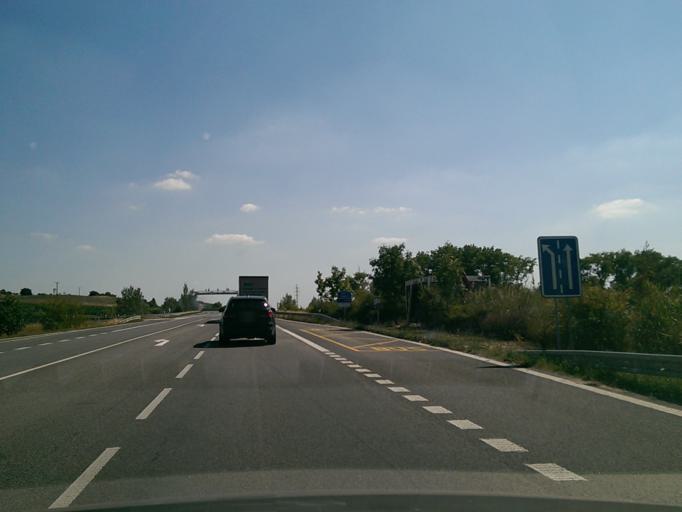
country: CZ
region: South Moravian
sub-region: Okres Breclav
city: Dolni Dunajovice
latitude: 48.8310
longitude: 16.6127
